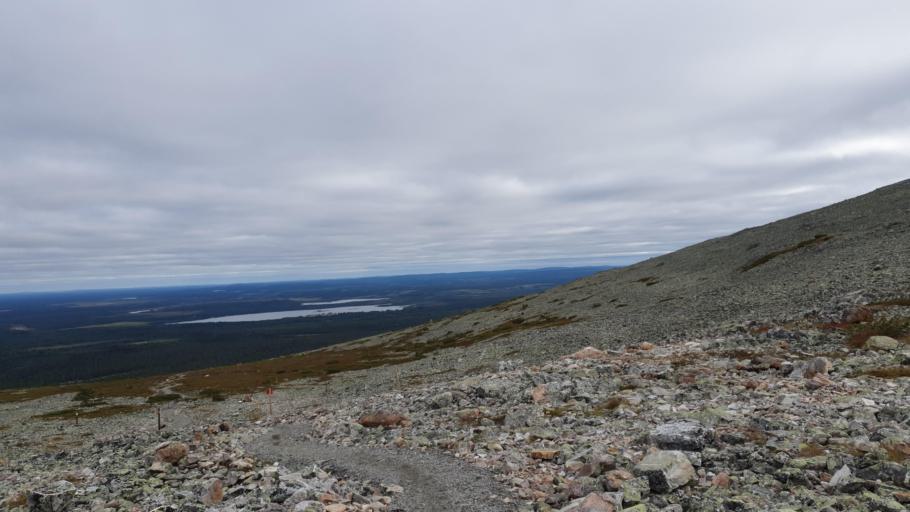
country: FI
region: Lapland
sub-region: Tunturi-Lappi
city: Kolari
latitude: 67.5681
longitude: 24.2454
